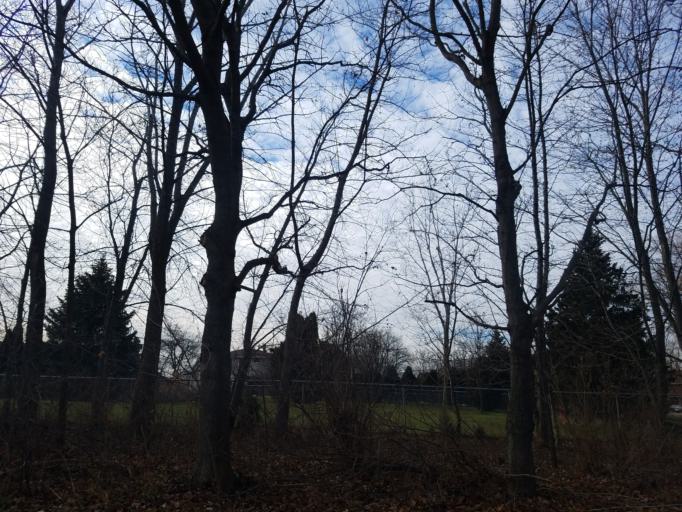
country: US
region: Illinois
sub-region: Will County
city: Homer Glen
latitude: 41.5705
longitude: -87.9436
